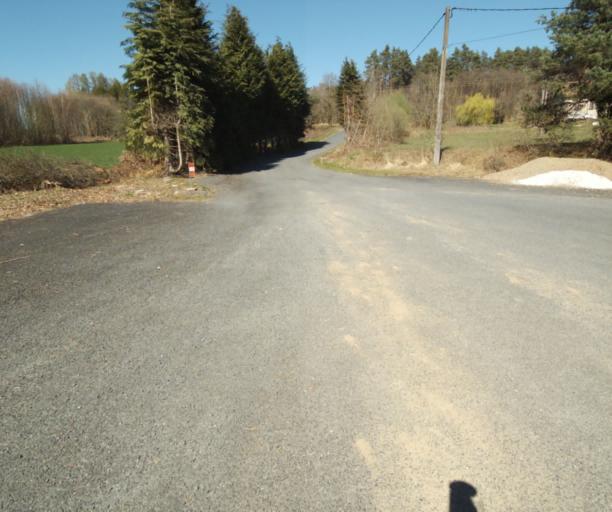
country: FR
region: Limousin
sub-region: Departement de la Correze
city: Chameyrat
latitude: 45.2682
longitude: 1.6928
